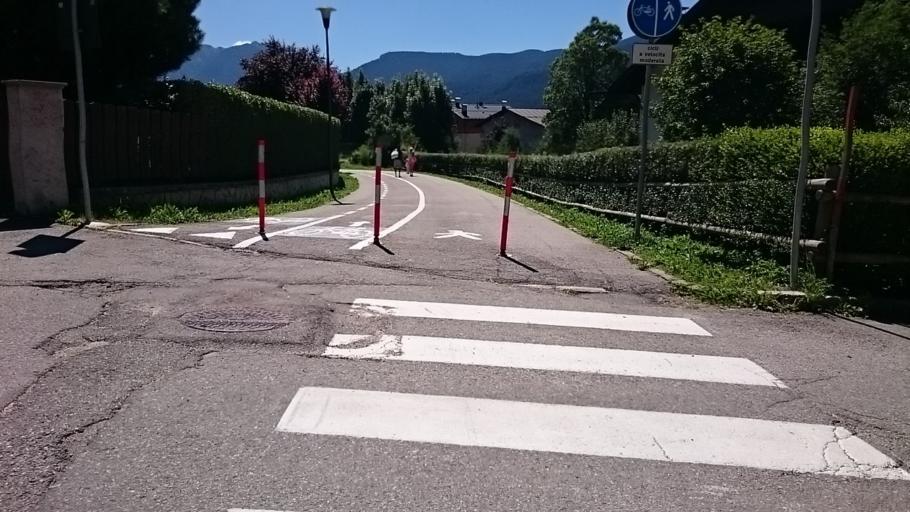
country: IT
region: Veneto
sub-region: Provincia di Belluno
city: San Vito
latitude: 46.4571
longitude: 12.2069
